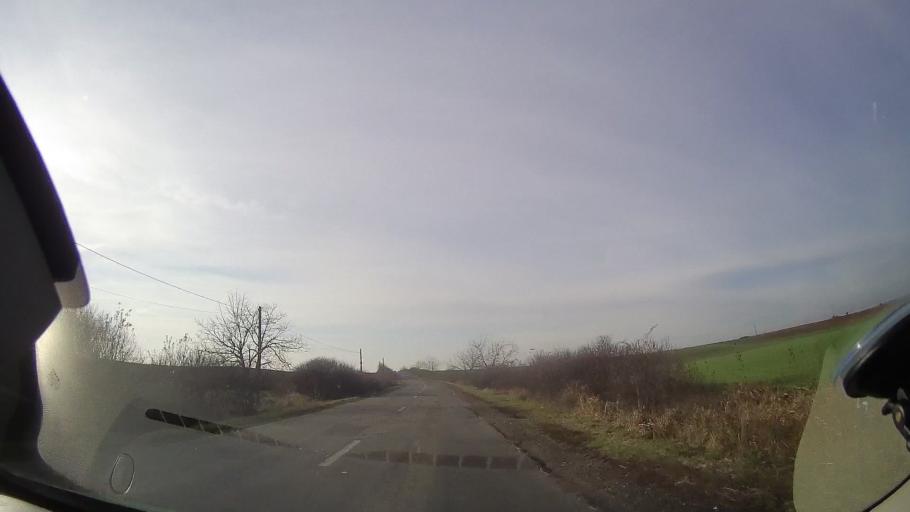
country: RO
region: Bihor
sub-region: Comuna Ciuhoiu
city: Ciuhoiu
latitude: 47.2264
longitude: 22.1445
